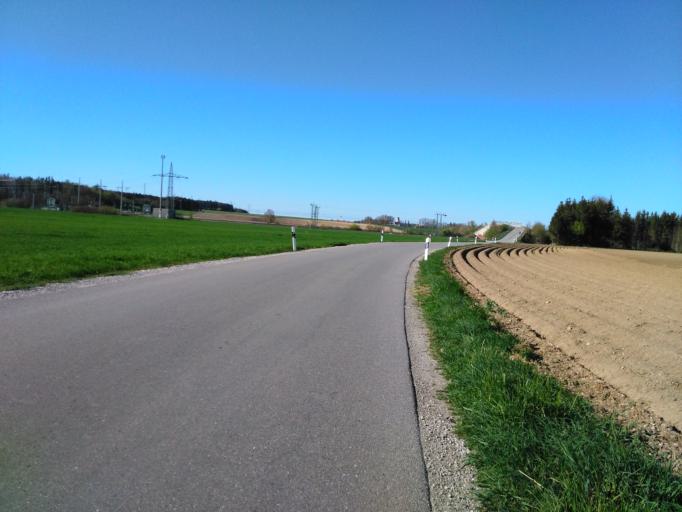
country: DE
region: Bavaria
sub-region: Upper Bavaria
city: Oberschweinbach
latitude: 48.2140
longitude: 11.1904
